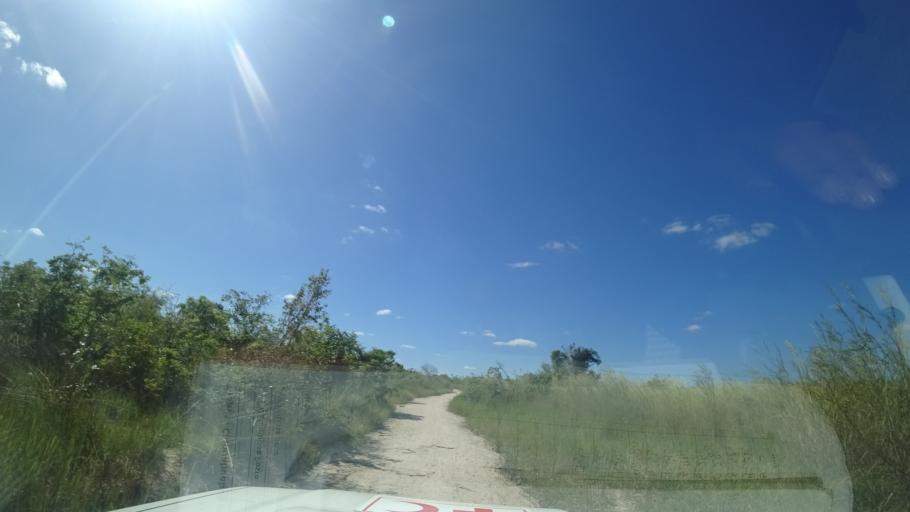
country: MZ
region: Sofala
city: Dondo
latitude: -19.4789
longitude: 34.6265
